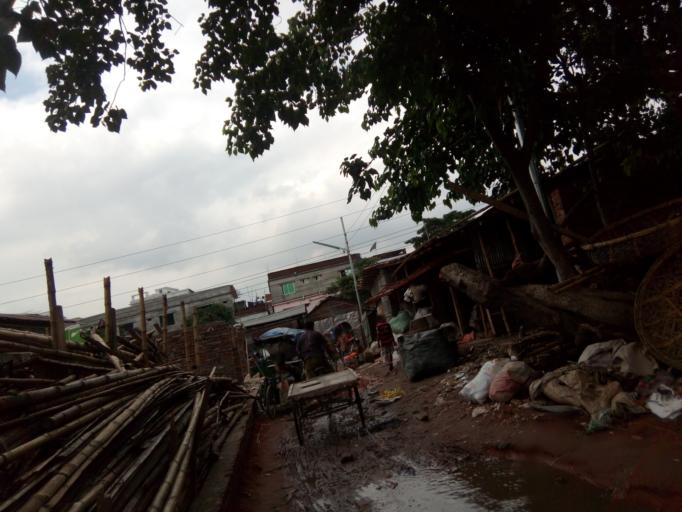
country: BD
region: Dhaka
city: Azimpur
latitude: 23.7488
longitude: 90.3614
